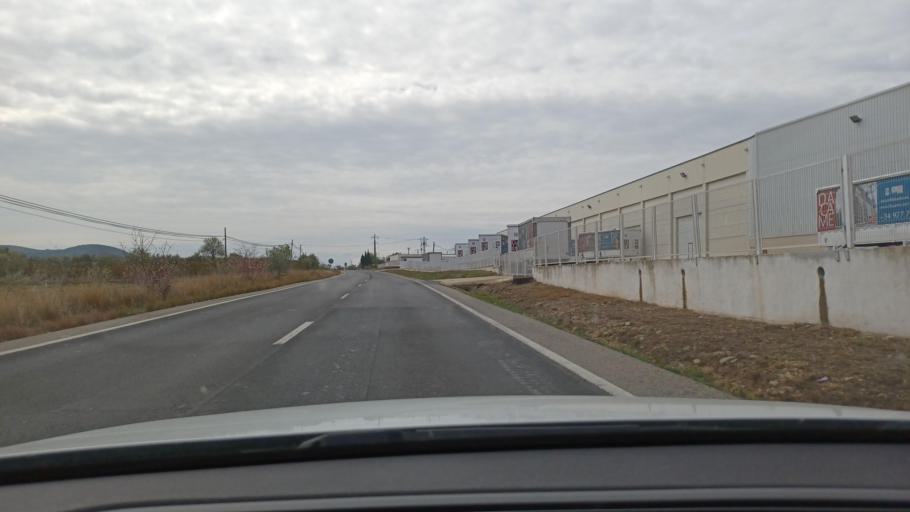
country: ES
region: Catalonia
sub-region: Provincia de Tarragona
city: Santa Barbara
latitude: 40.6897
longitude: 0.4720
